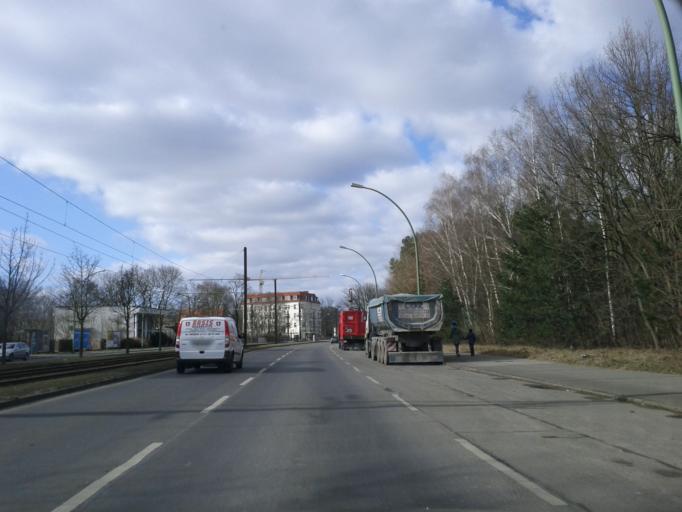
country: DE
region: Berlin
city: Adlershof
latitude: 52.4560
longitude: 13.5532
